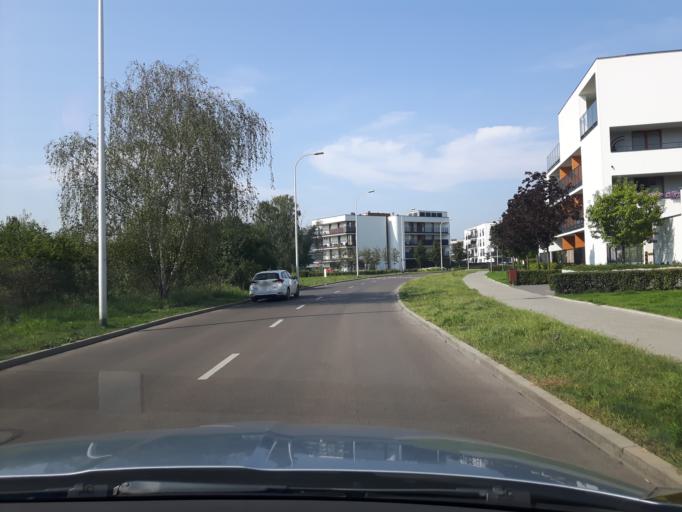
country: PL
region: Masovian Voivodeship
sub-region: Powiat wolominski
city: Zabki
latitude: 52.2739
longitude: 21.0829
